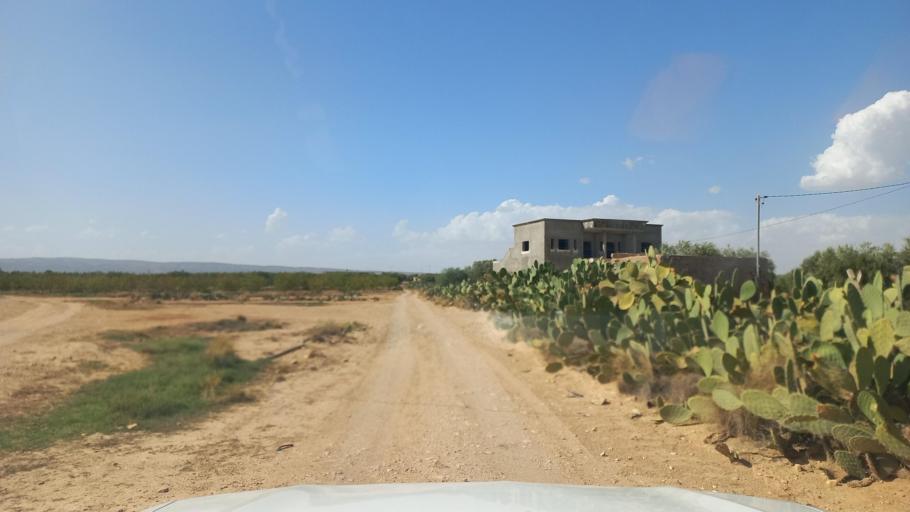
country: TN
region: Al Qasrayn
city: Kasserine
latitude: 35.2694
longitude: 9.0246
